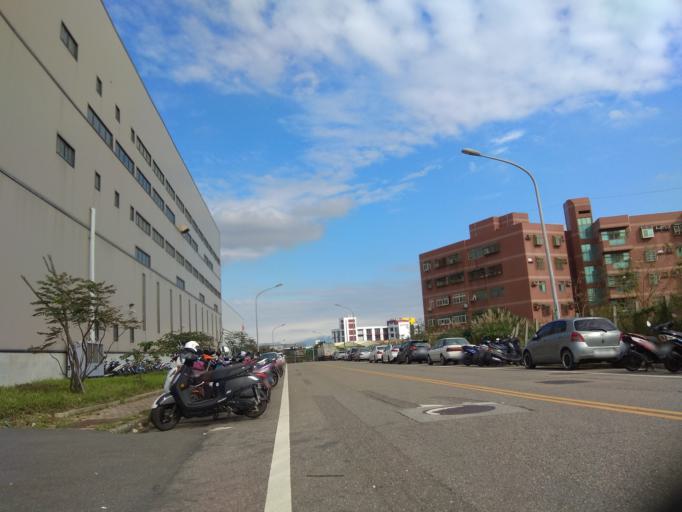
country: TW
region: Taiwan
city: Taoyuan City
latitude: 25.0587
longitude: 121.1771
